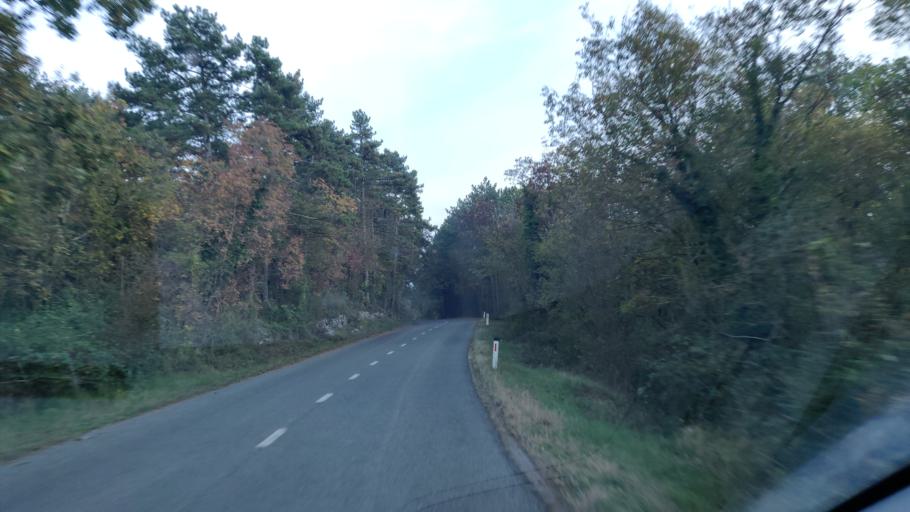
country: IT
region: Friuli Venezia Giulia
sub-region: Provincia di Trieste
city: Zolla
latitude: 45.7996
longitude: 13.8520
